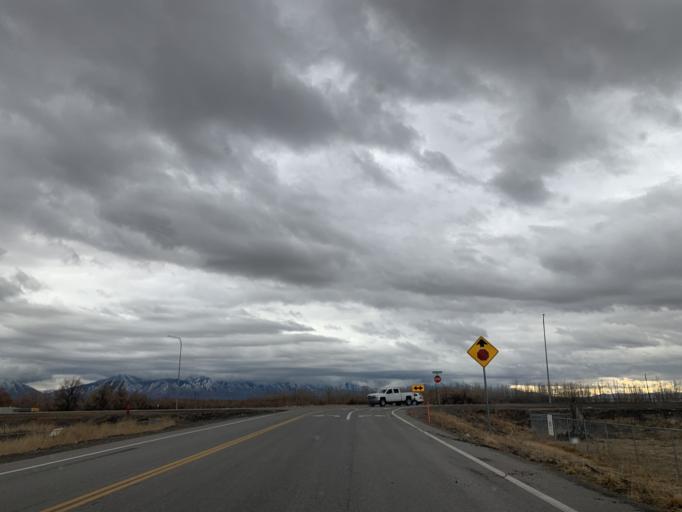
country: US
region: Utah
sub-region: Utah County
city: Provo
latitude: 40.2111
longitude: -111.6777
